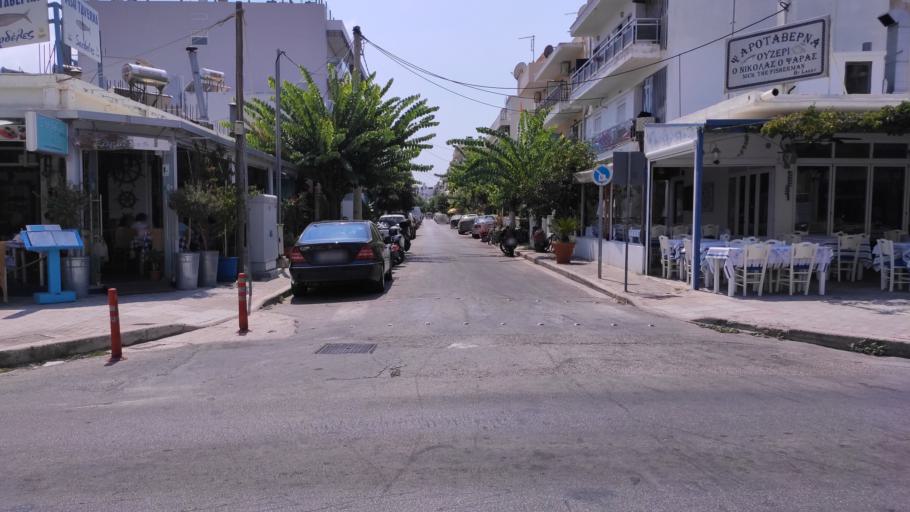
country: GR
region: South Aegean
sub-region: Nomos Dodekanisou
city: Kos
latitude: 36.8986
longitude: 27.2865
